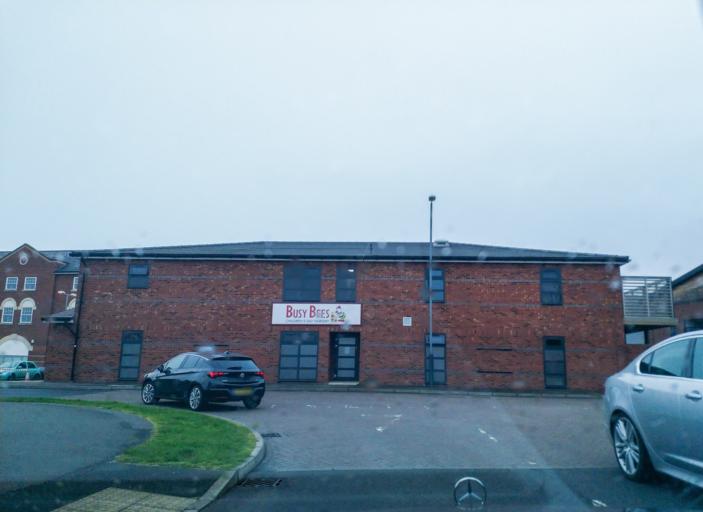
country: GB
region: England
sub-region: Warwickshire
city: Warwick
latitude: 52.2695
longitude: -1.6085
